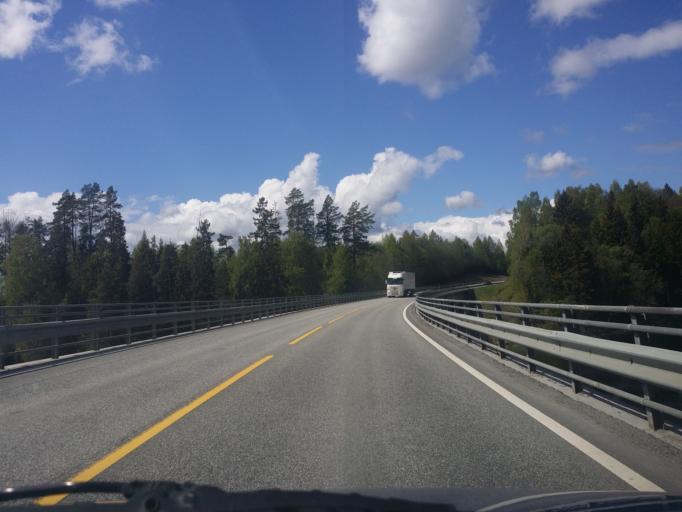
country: NO
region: Buskerud
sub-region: Ringerike
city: Honefoss
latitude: 60.1457
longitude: 10.2330
